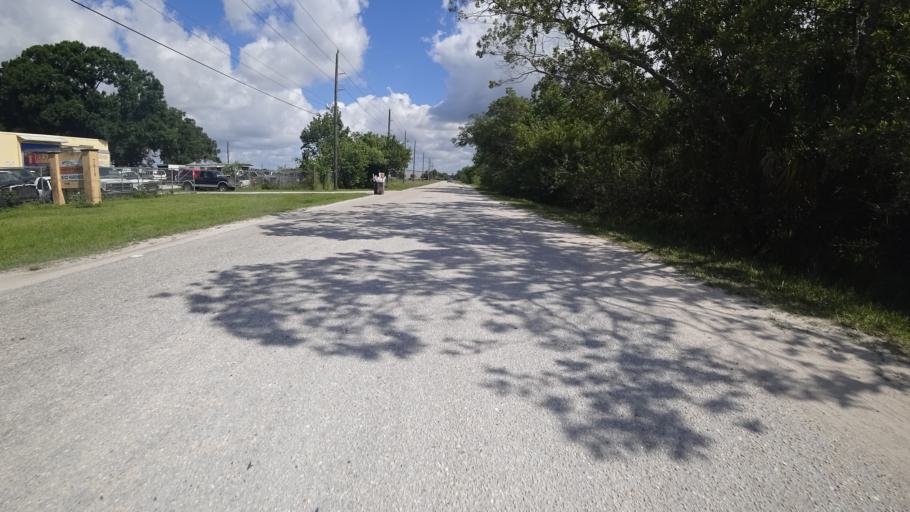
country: US
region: Florida
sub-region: Manatee County
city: Whitfield
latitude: 27.4157
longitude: -82.5282
